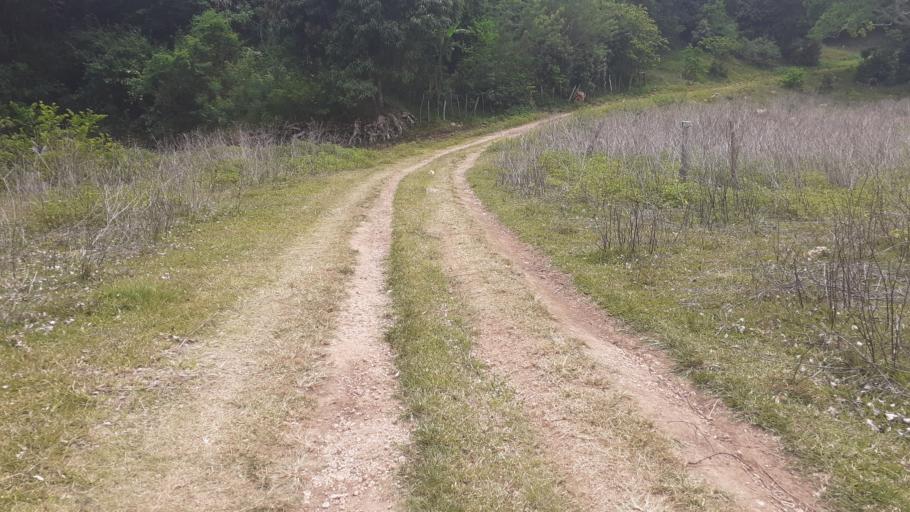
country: VU
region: Tafea
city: Isangel
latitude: -18.8192
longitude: 169.0240
